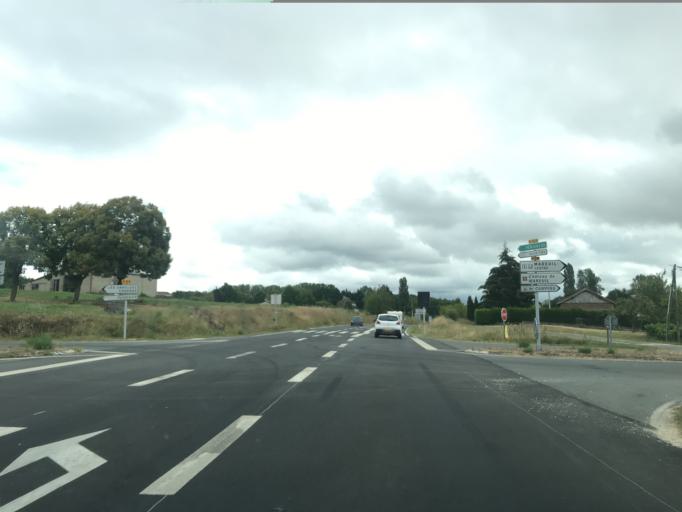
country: FR
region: Aquitaine
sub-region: Departement de la Dordogne
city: Mareuil
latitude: 45.4546
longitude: 0.4528
